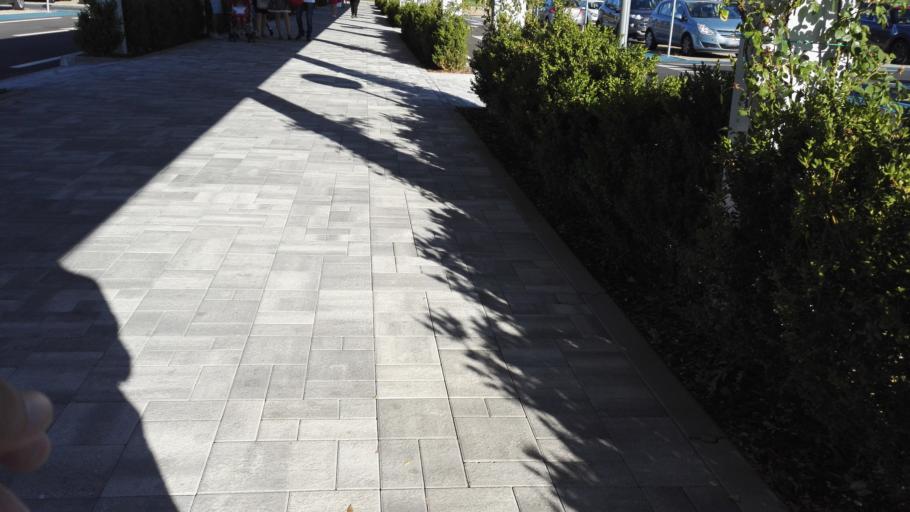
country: IT
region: Lombardy
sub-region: Citta metropolitana di Milano
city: Locate di Triulzi
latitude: 45.3598
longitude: 9.2192
